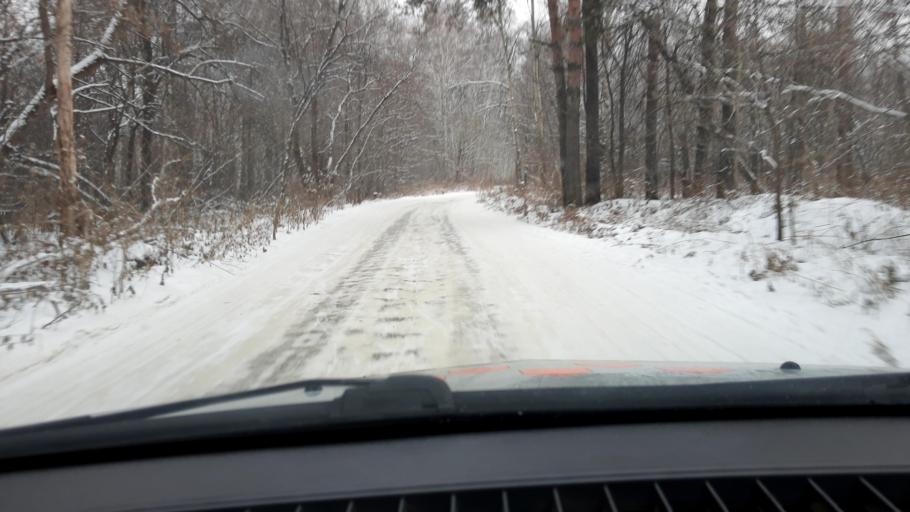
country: RU
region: Bashkortostan
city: Iglino
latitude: 54.8319
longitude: 56.1998
